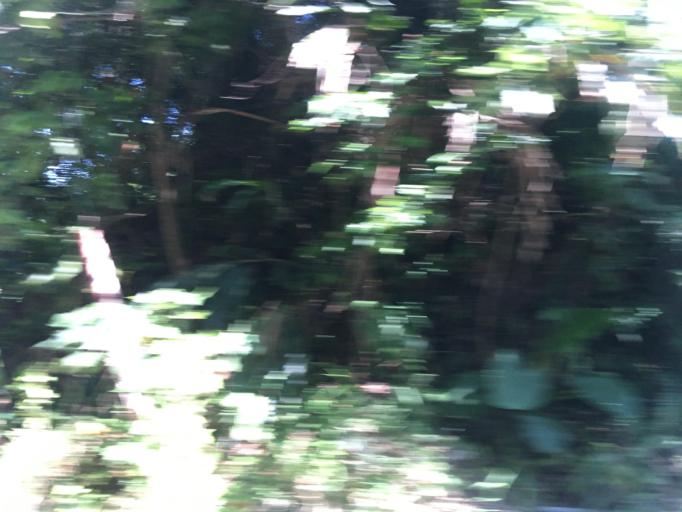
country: TW
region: Taiwan
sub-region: Yilan
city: Yilan
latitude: 24.4405
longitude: 121.7654
